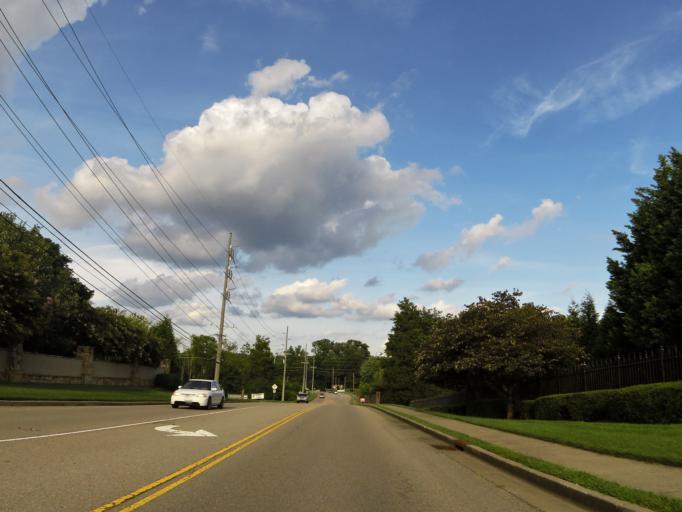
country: US
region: Tennessee
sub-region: Blount County
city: Louisville
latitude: 35.8914
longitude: -84.0711
